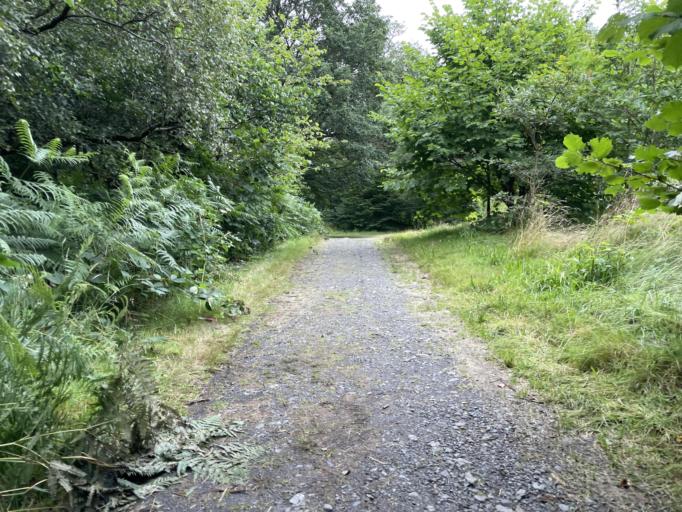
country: GB
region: Scotland
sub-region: Dumfries and Galloway
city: Newton Stewart
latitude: 55.0804
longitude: -4.5055
